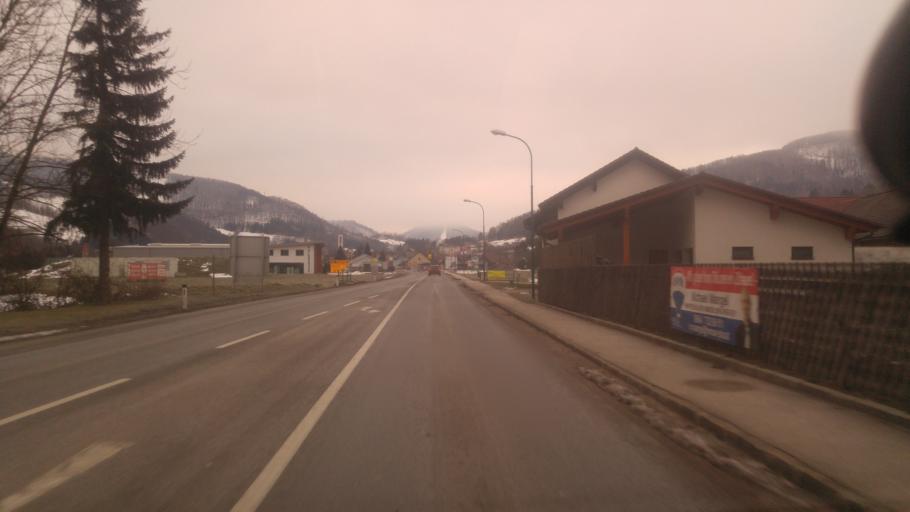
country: AT
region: Lower Austria
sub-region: Politischer Bezirk Lilienfeld
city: Traisen
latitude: 48.0480
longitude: 15.6099
